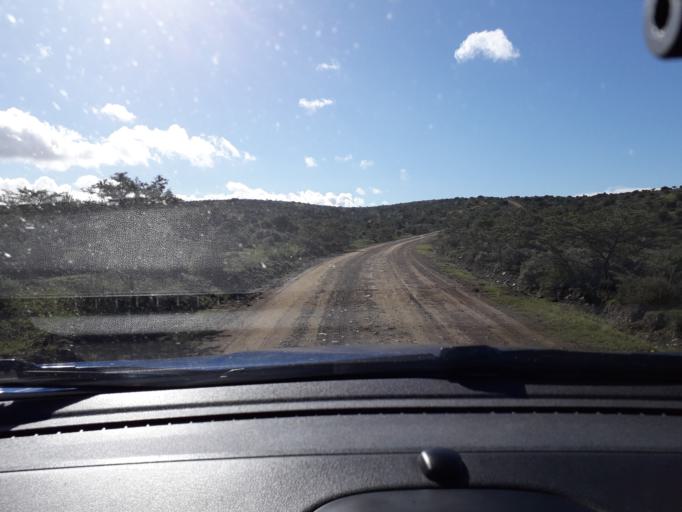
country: ZA
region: Eastern Cape
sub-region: Buffalo City Metropolitan Municipality
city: Bhisho
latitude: -33.1221
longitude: 27.4519
